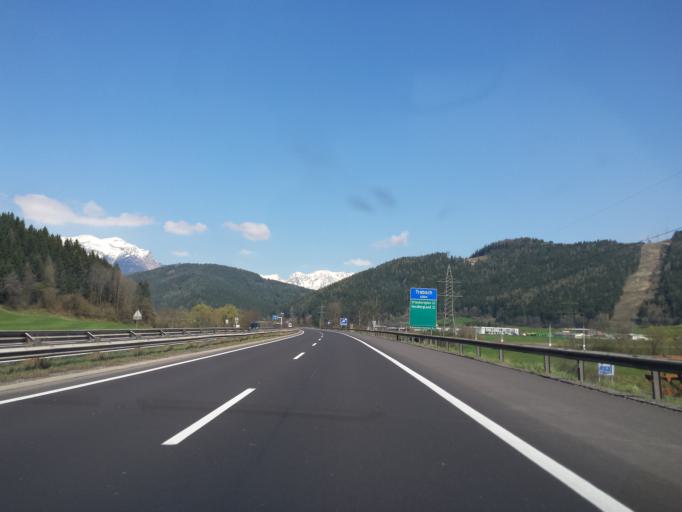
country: AT
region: Styria
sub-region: Politischer Bezirk Leoben
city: Traboch
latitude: 47.3623
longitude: 14.9990
